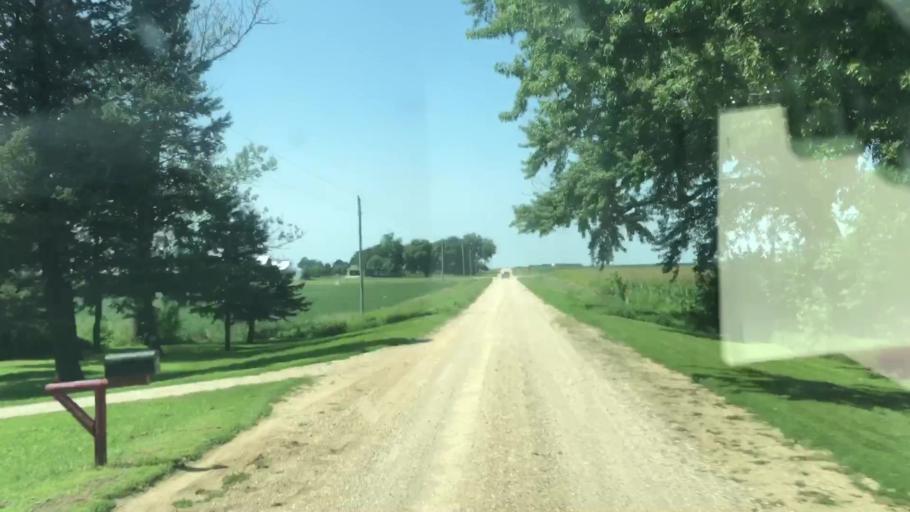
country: US
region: Iowa
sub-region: O'Brien County
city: Sanborn
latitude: 43.2006
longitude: -95.7204
